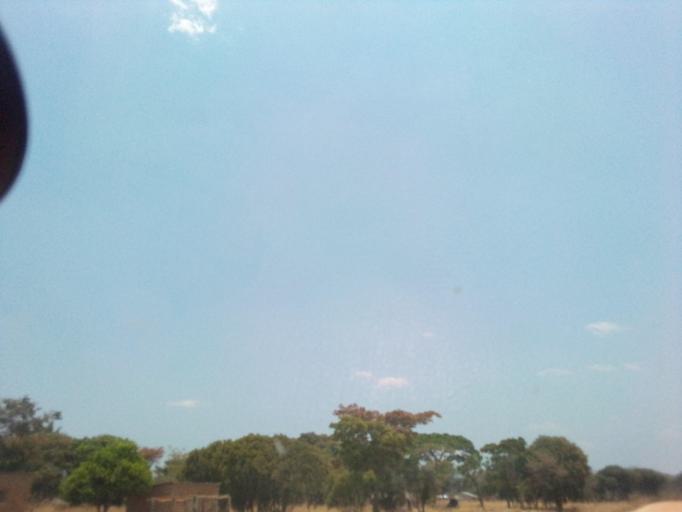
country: ZM
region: Northern
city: Chinsali
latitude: -10.8561
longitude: 31.6760
